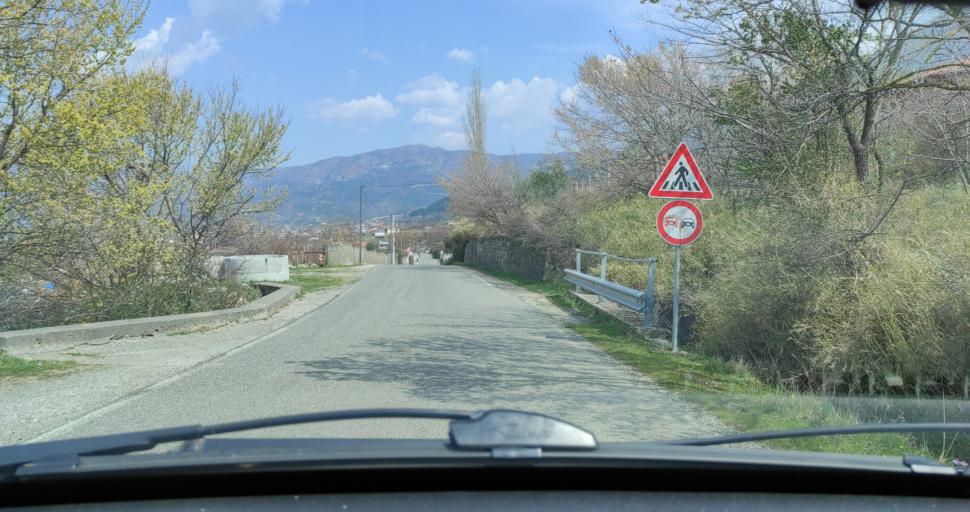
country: AL
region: Lezhe
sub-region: Rrethi i Lezhes
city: Kallmeti i Madh
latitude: 41.8420
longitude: 19.6783
